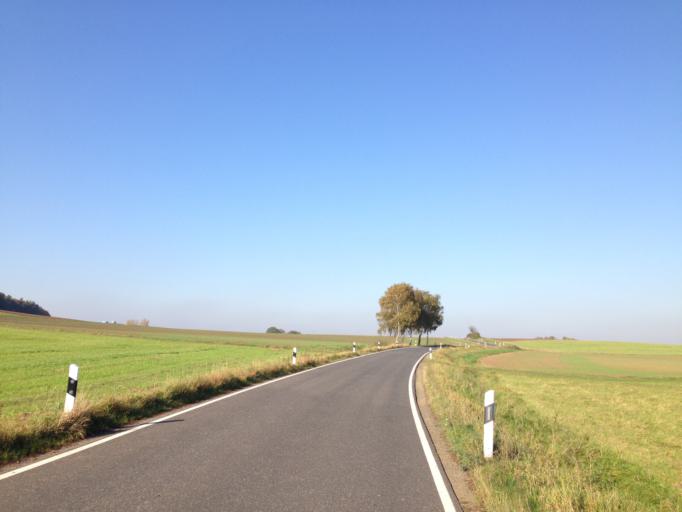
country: DE
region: Hesse
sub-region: Regierungsbezirk Giessen
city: Lich
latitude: 50.5619
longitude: 8.8081
